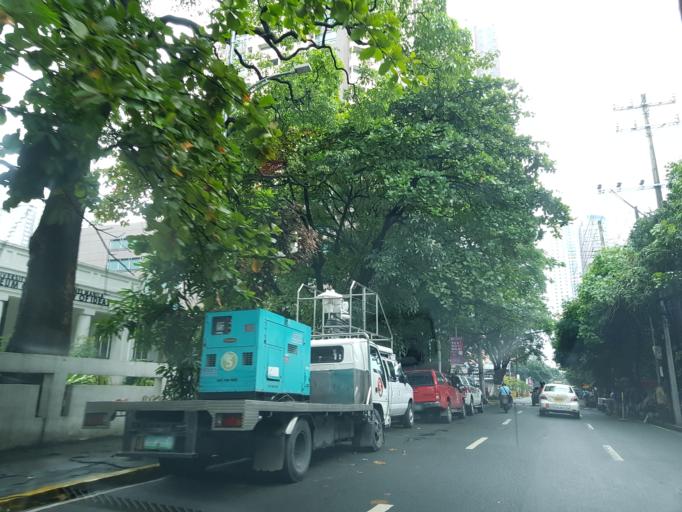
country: PH
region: Metro Manila
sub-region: City of Manila
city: Port Area
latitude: 14.5790
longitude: 120.9843
